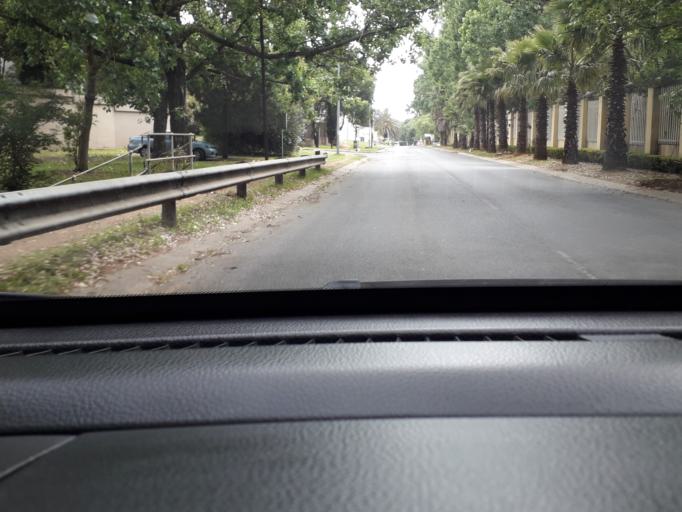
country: ZA
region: Gauteng
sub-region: City of Johannesburg Metropolitan Municipality
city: Modderfontein
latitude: -26.0963
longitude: 28.0715
